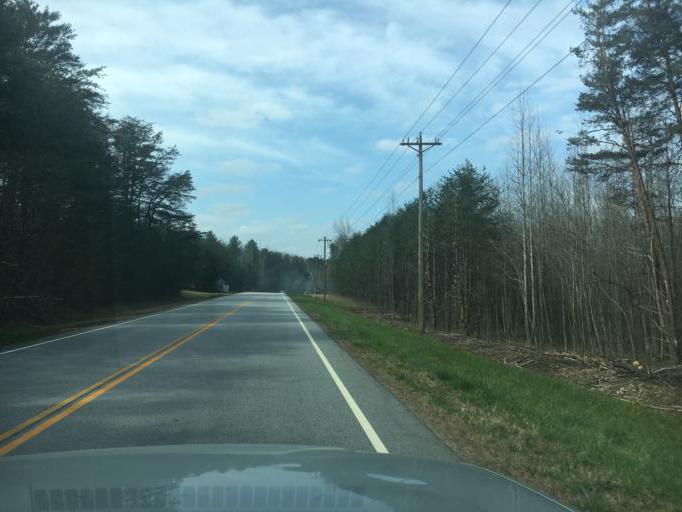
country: US
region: South Carolina
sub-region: Greenville County
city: Tigerville
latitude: 35.1241
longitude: -82.3223
